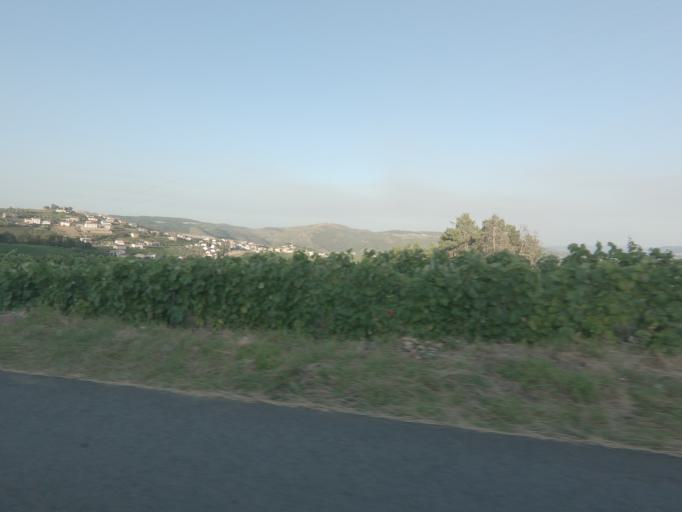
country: PT
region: Vila Real
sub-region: Sabrosa
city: Vilela
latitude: 41.2070
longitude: -7.6744
